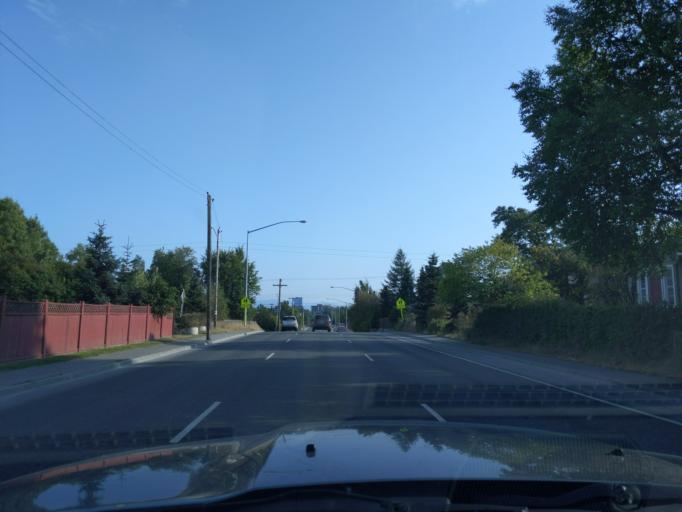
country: US
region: Alaska
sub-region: Anchorage Municipality
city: Anchorage
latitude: 61.2121
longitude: -149.8873
